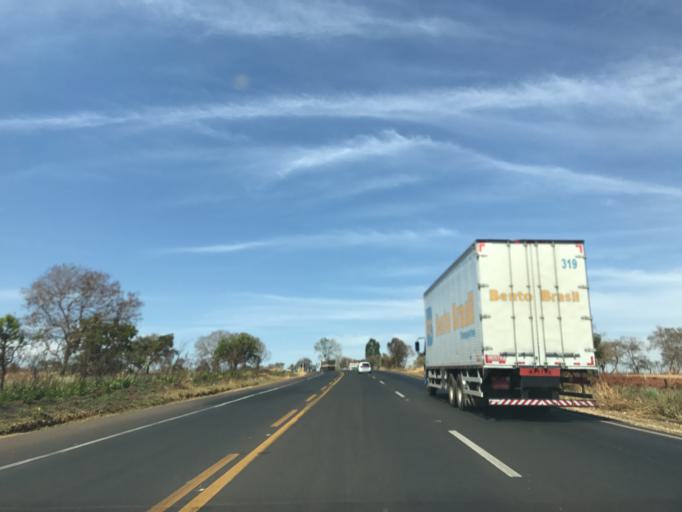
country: BR
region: Minas Gerais
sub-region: Monte Alegre De Minas
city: Monte Alegre de Minas
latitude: -18.9547
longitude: -49.0281
